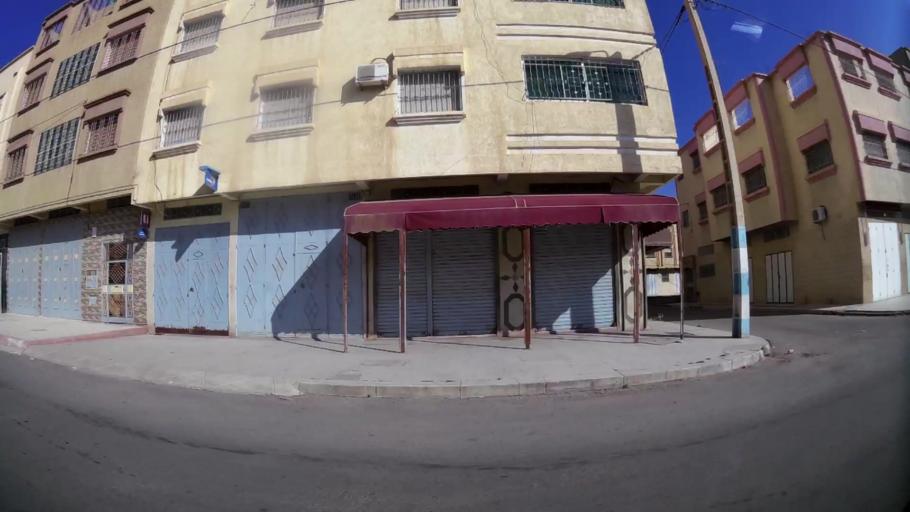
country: MA
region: Oriental
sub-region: Oujda-Angad
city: Oujda
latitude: 34.6786
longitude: -1.9332
